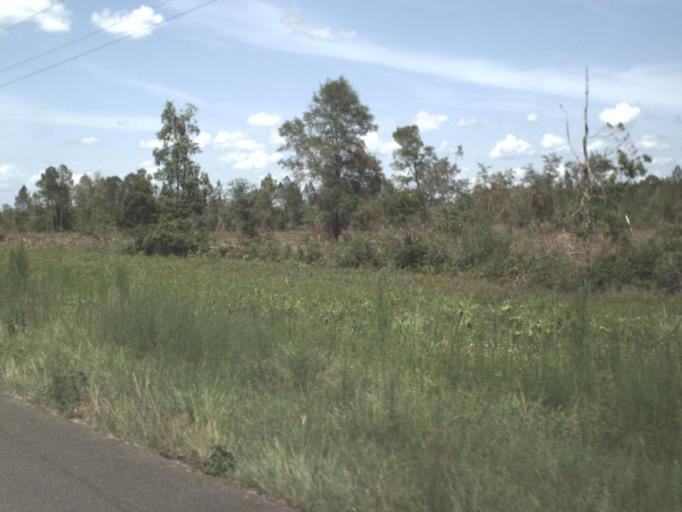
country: US
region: Florida
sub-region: Gilchrist County
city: Trenton
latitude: 29.6877
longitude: -82.7650
